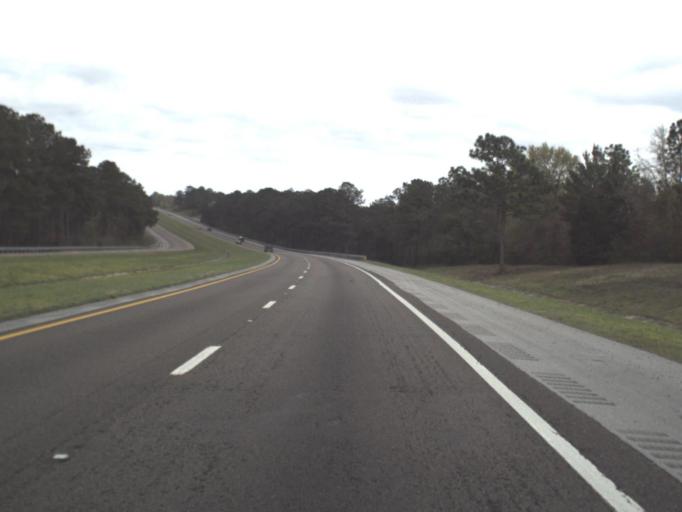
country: US
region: Florida
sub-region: Walton County
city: DeFuniak Springs
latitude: 30.7268
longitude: -86.2107
